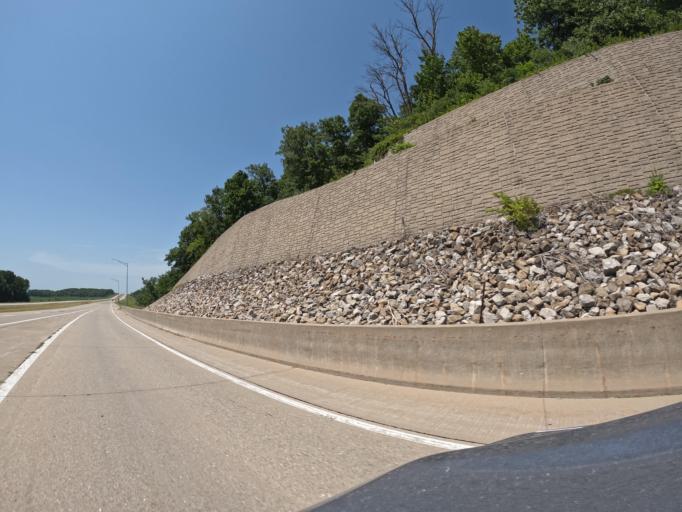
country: US
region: Iowa
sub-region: Henry County
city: Mount Pleasant
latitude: 40.9702
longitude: -91.6390
